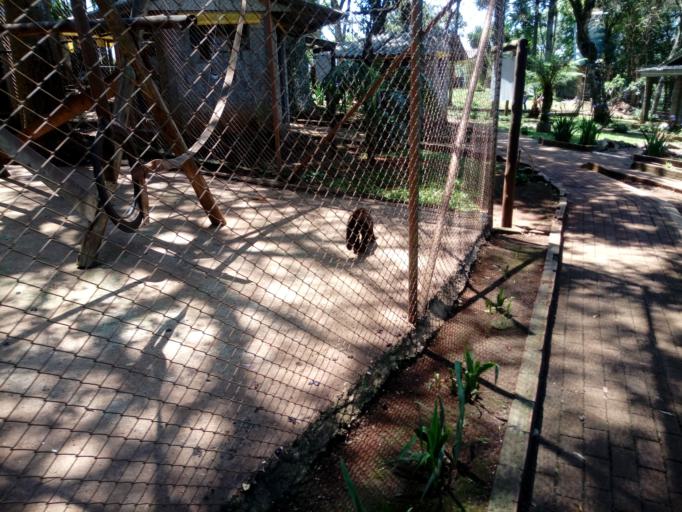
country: BR
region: Santa Catarina
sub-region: Chapeco
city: Chapeco
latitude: -27.2097
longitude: -52.6333
